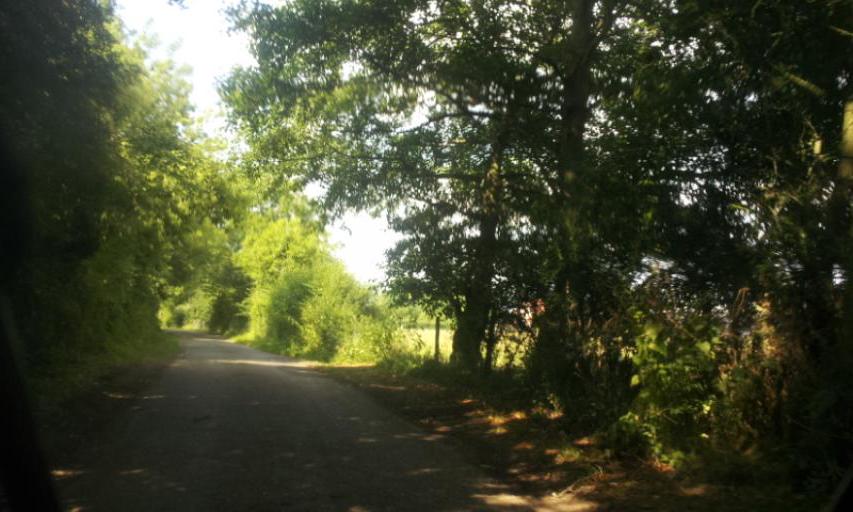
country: GB
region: England
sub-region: Kent
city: Yalding
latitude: 51.2034
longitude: 0.4292
